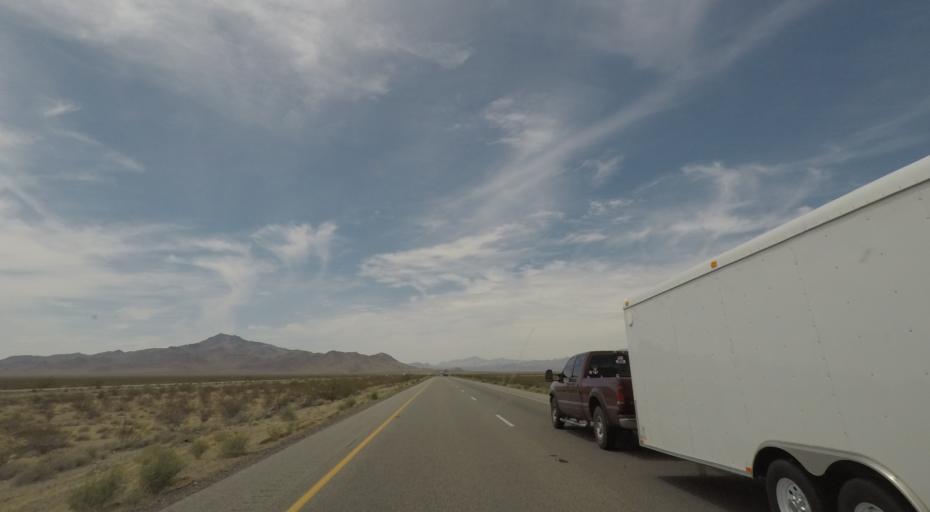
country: US
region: California
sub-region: San Bernardino County
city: Needles
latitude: 34.8052
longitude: -115.2718
